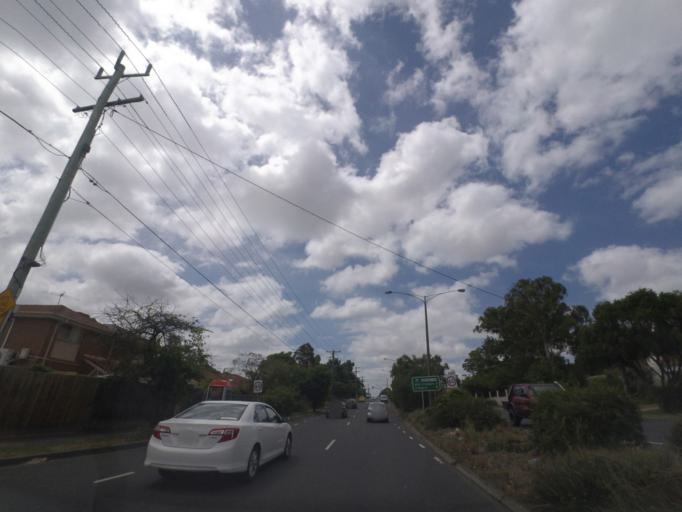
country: AU
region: Victoria
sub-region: Maroondah
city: Croydon North
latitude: -37.7991
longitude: 145.2899
